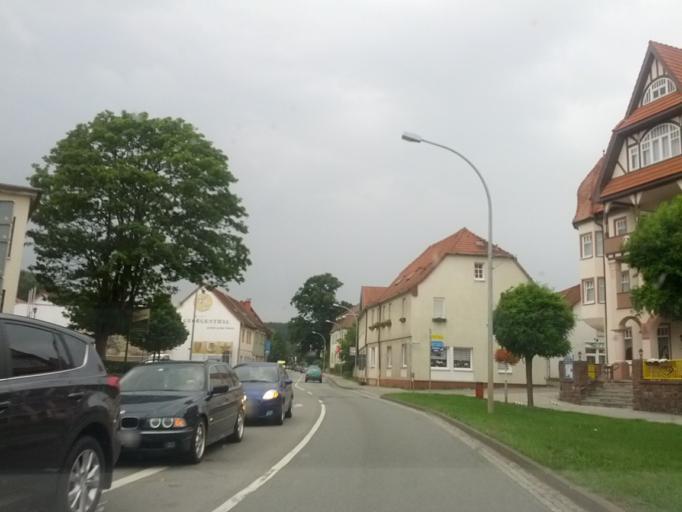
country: DE
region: Thuringia
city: Georgenthal
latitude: 50.8295
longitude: 10.6571
